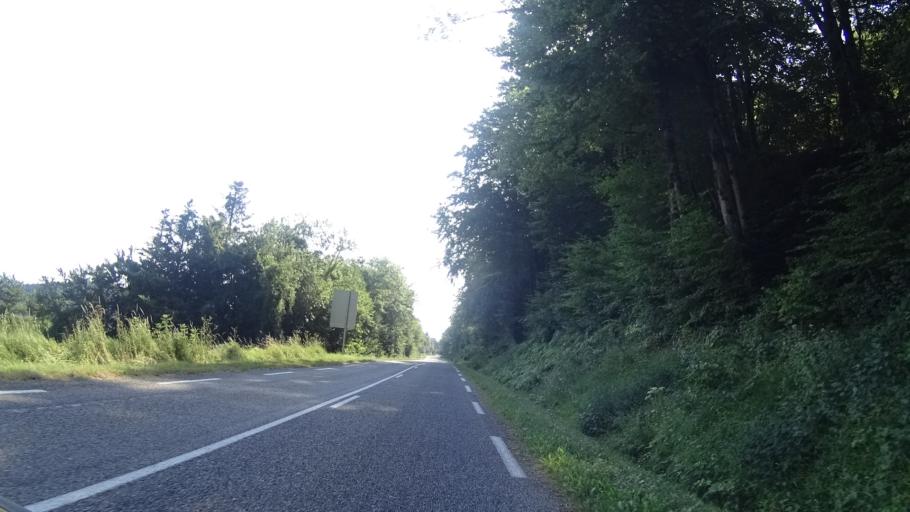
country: FR
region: Midi-Pyrenees
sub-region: Departement de l'Ariege
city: Belesta
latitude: 42.9111
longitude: 1.9831
